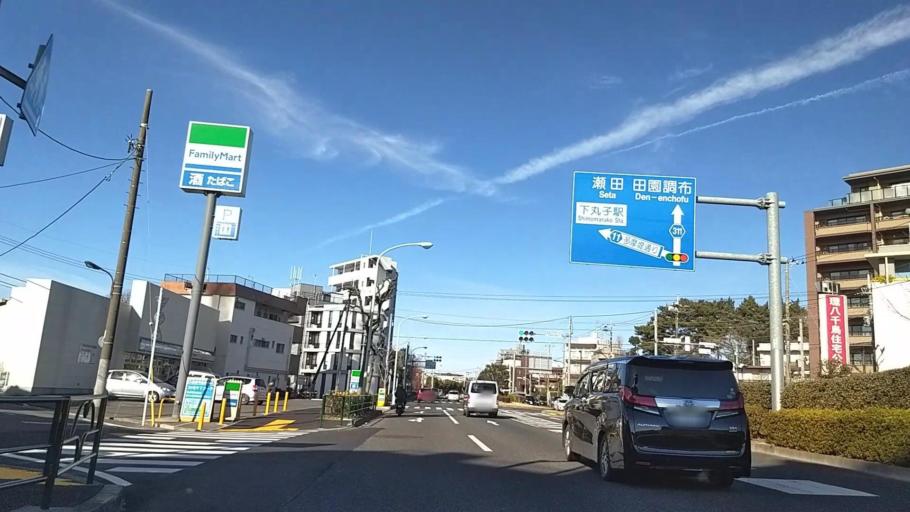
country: JP
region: Kanagawa
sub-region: Kawasaki-shi
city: Kawasaki
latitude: 35.5718
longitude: 139.6877
